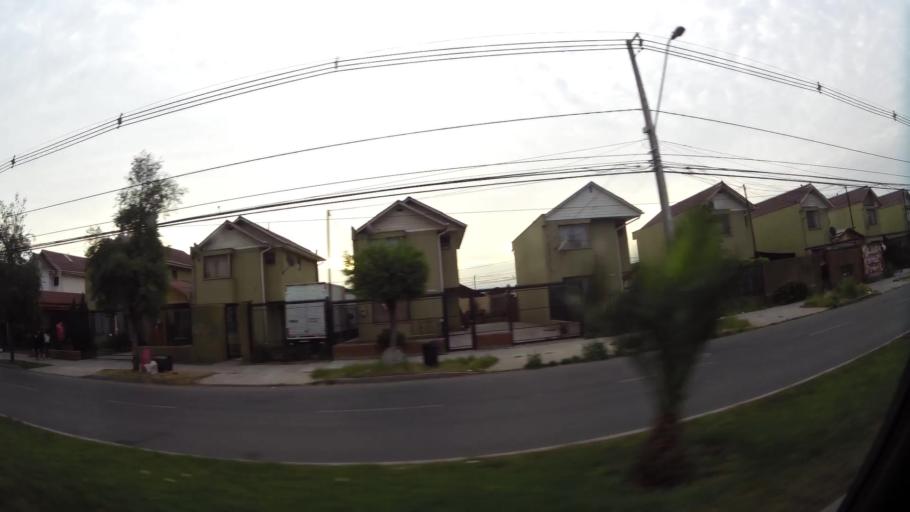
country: CL
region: Santiago Metropolitan
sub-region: Provincia de Santiago
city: Lo Prado
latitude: -33.5301
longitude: -70.7927
